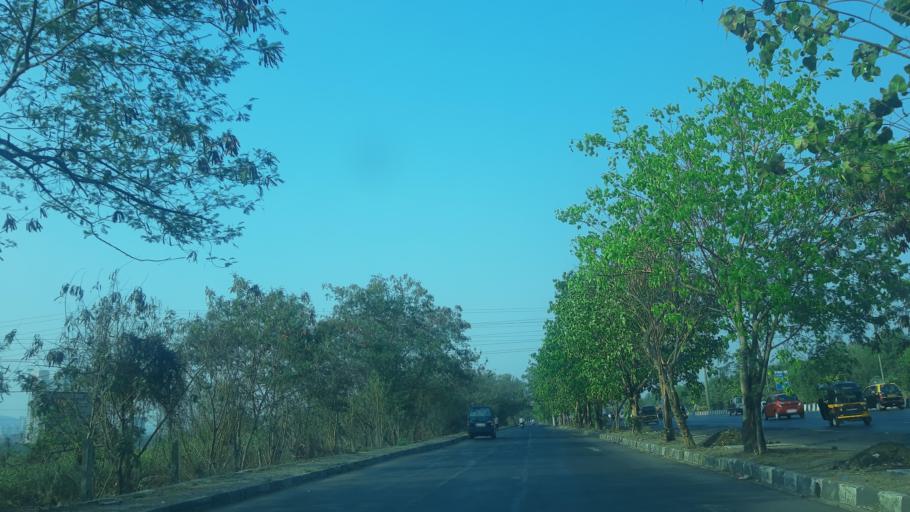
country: IN
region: Maharashtra
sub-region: Thane
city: Airoli
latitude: 19.1463
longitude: 72.9512
